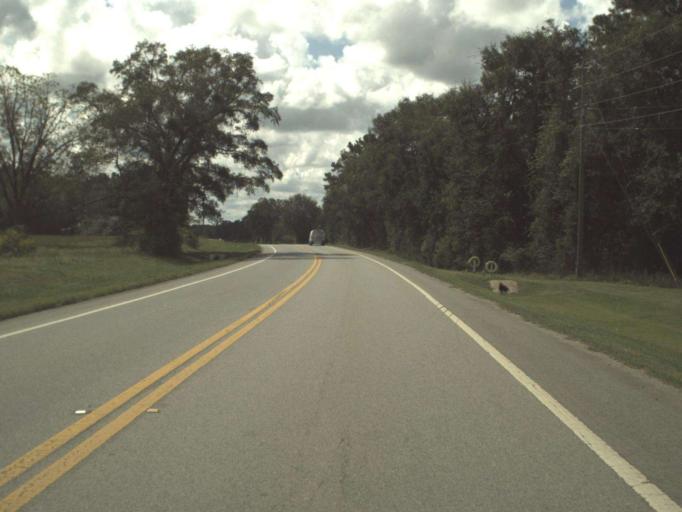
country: US
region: Florida
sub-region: Jackson County
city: Graceville
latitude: 30.9230
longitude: -85.4278
